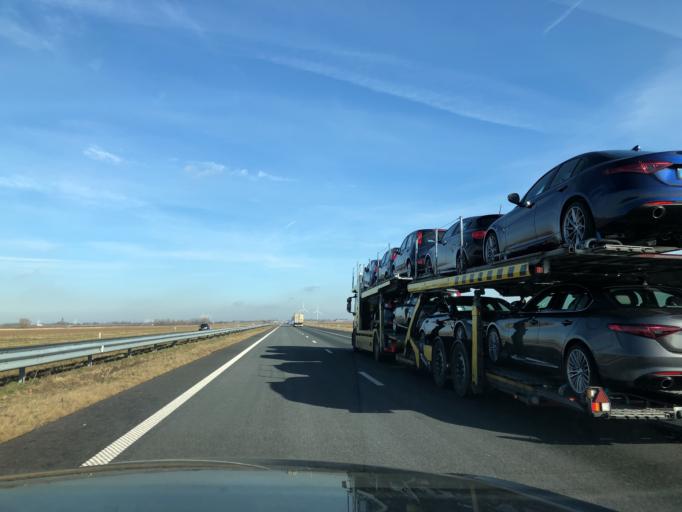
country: NL
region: North Brabant
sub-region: Gemeente Steenbergen
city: Dinteloord
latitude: 51.6067
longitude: 4.3699
